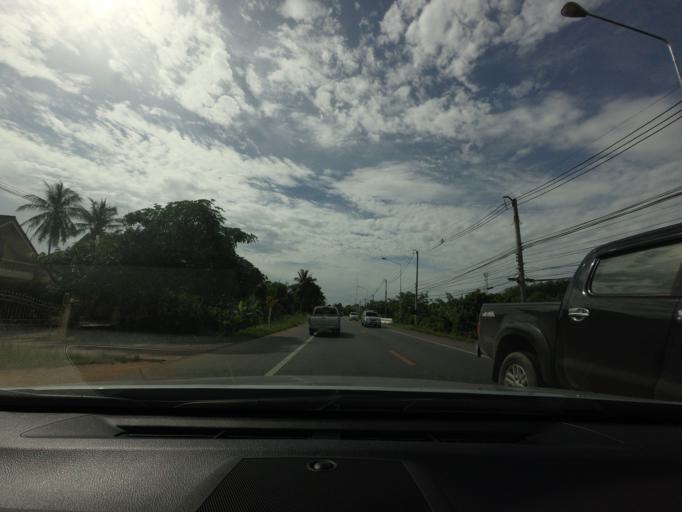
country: TH
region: Songkhla
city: Khlong Hoi Khong
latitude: 6.9200
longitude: 100.4109
